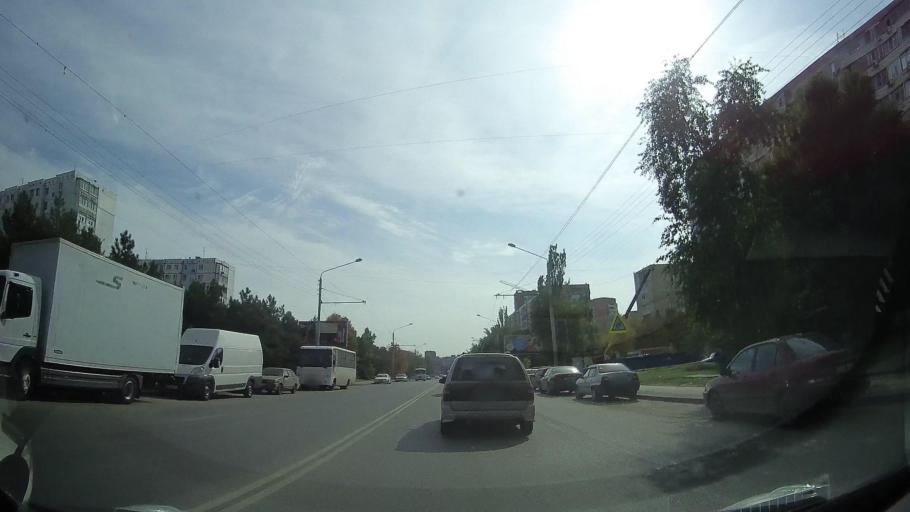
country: RU
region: Rostov
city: Severnyy
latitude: 47.2926
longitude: 39.7031
